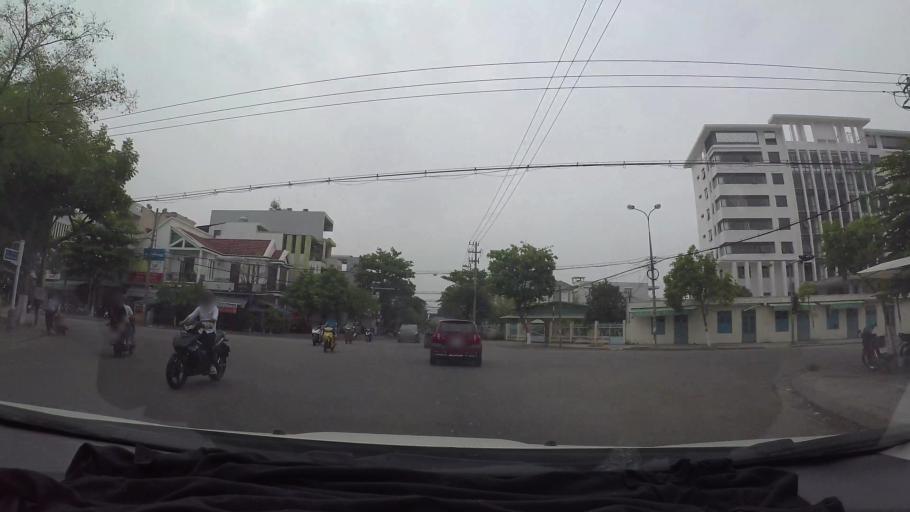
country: VN
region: Da Nang
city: Cam Le
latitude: 16.0361
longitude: 108.2143
